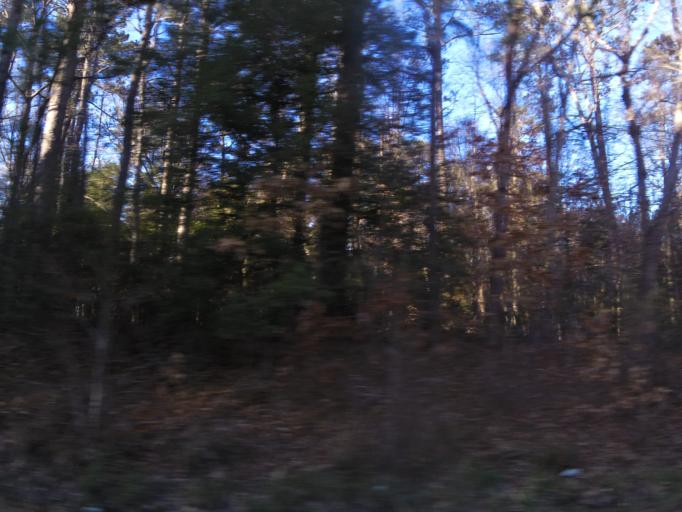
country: US
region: Virginia
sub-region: City of Franklin
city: Franklin
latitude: 36.6487
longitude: -76.8711
